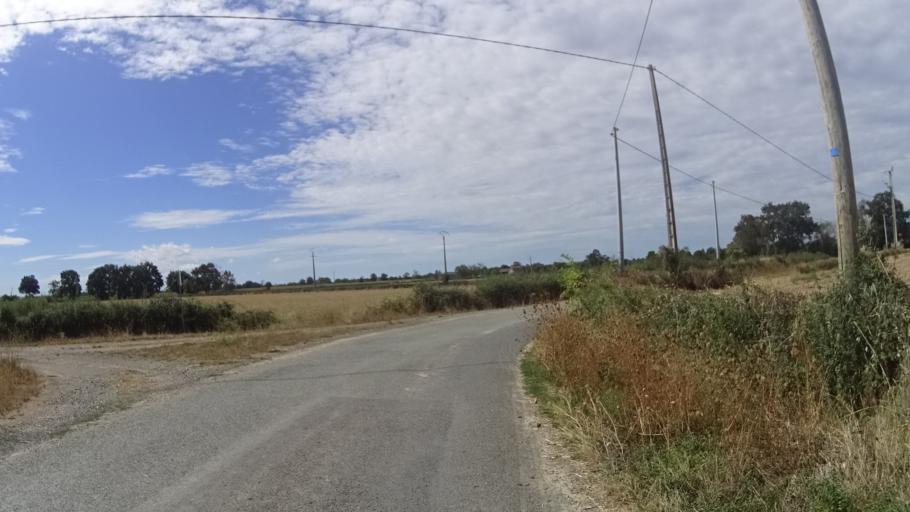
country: FR
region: Auvergne
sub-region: Departement de l'Allier
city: Beaulon
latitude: 46.6489
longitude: 3.6831
